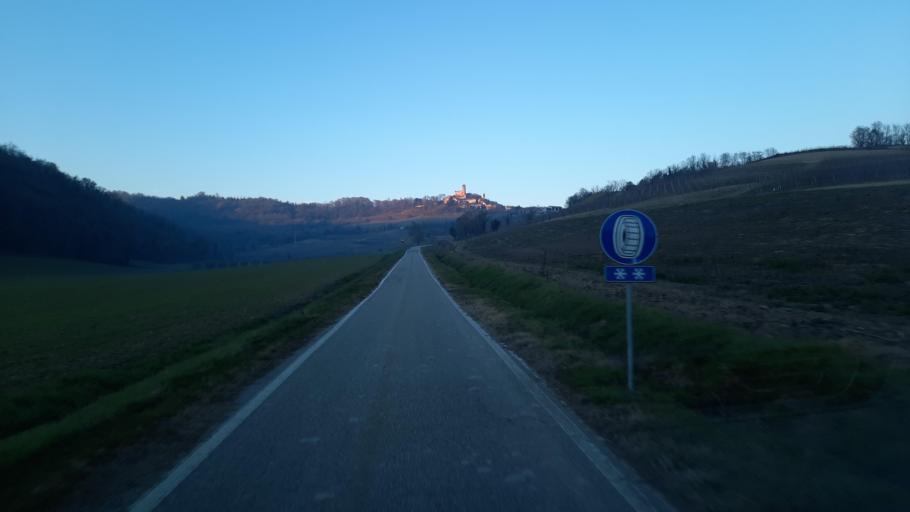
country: IT
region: Piedmont
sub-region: Provincia di Alessandria
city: Camino
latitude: 45.1512
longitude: 8.2826
